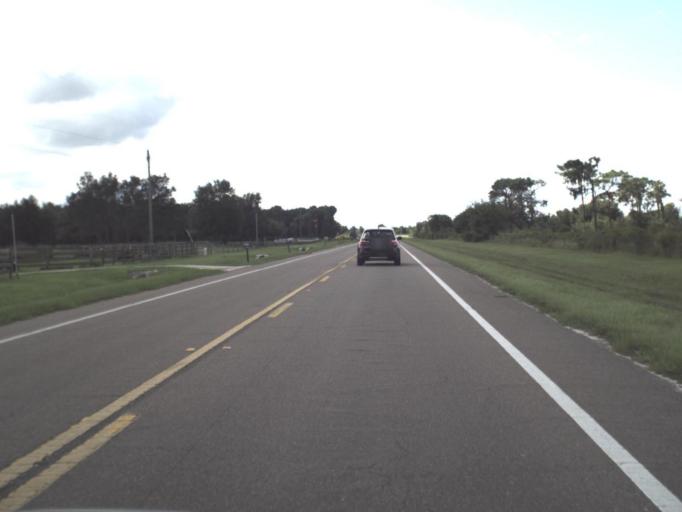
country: US
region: Florida
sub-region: DeSoto County
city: Arcadia
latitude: 27.2951
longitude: -82.0648
